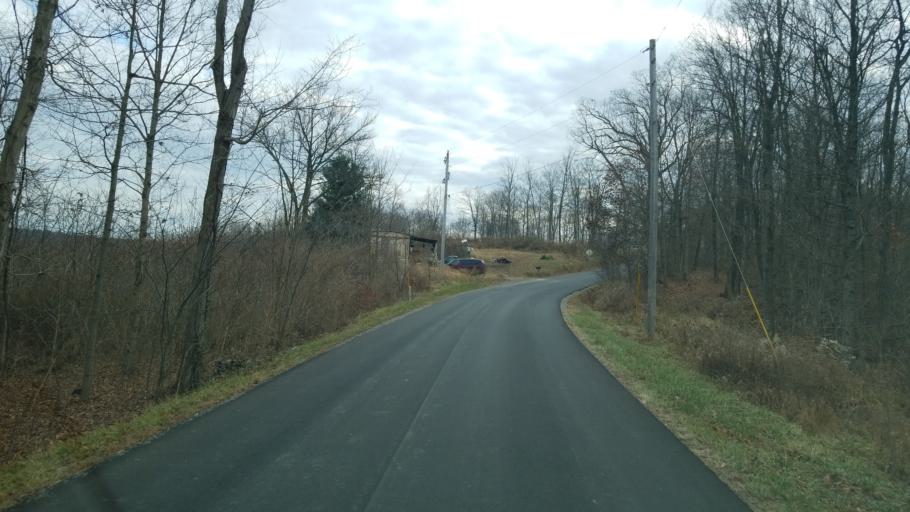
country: US
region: Ohio
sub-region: Highland County
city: Greenfield
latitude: 39.1973
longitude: -83.2656
